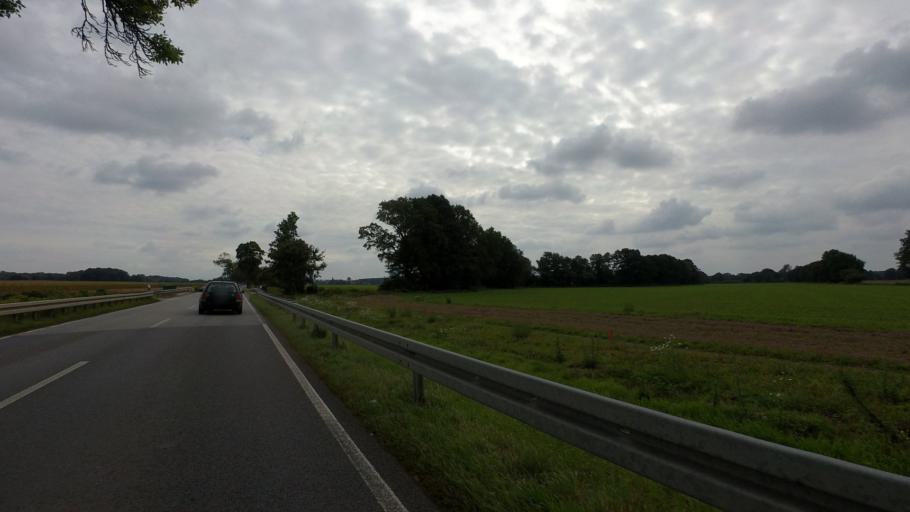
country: DE
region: Brandenburg
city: Golssen
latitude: 51.9604
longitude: 13.6259
